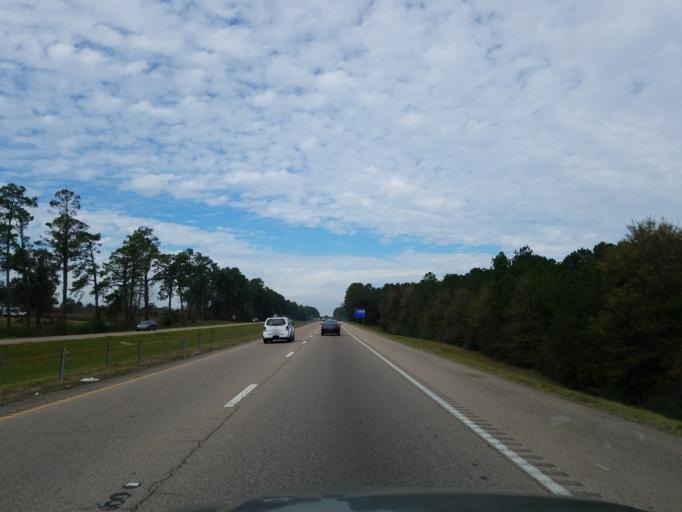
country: US
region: Mississippi
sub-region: Lamar County
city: West Hattiesburg
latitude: 31.2529
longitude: -89.3320
